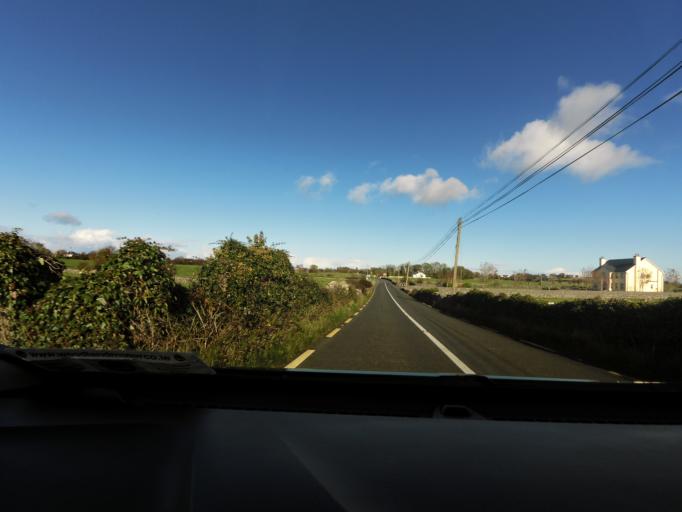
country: IE
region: Connaught
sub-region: Maigh Eo
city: Ballinrobe
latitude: 53.5728
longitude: -9.1206
